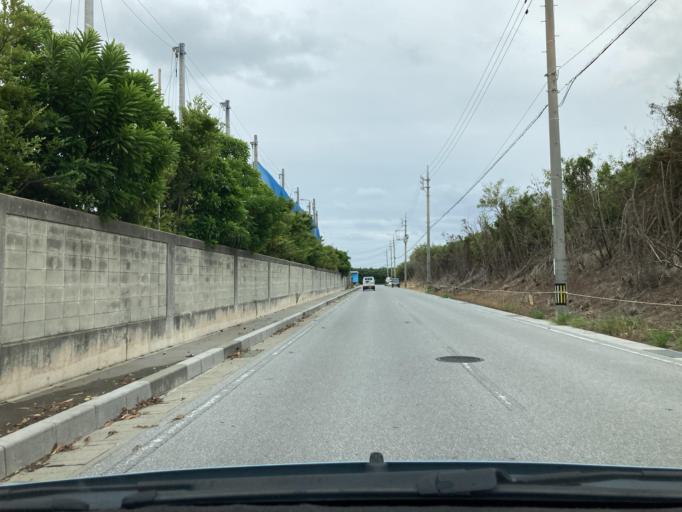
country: JP
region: Okinawa
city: Itoman
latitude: 26.1288
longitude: 127.6537
